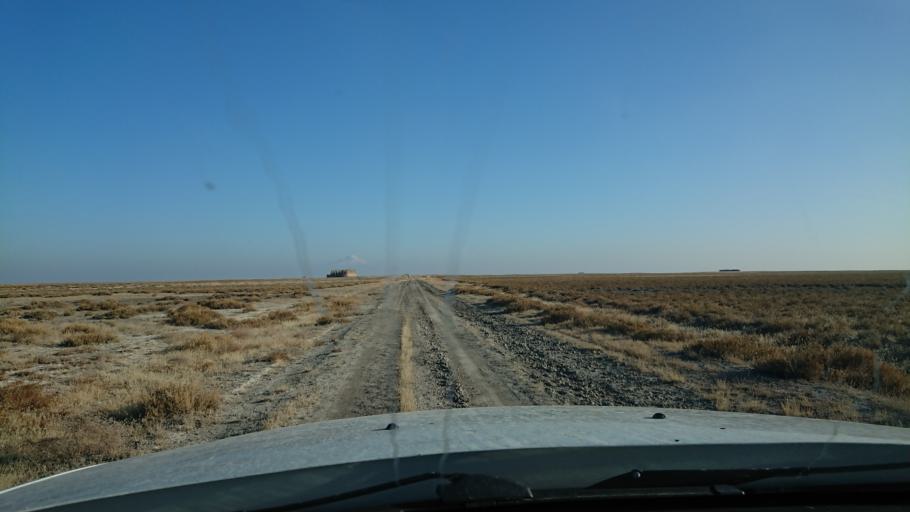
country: TR
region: Aksaray
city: Sultanhani
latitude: 38.3955
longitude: 33.5906
